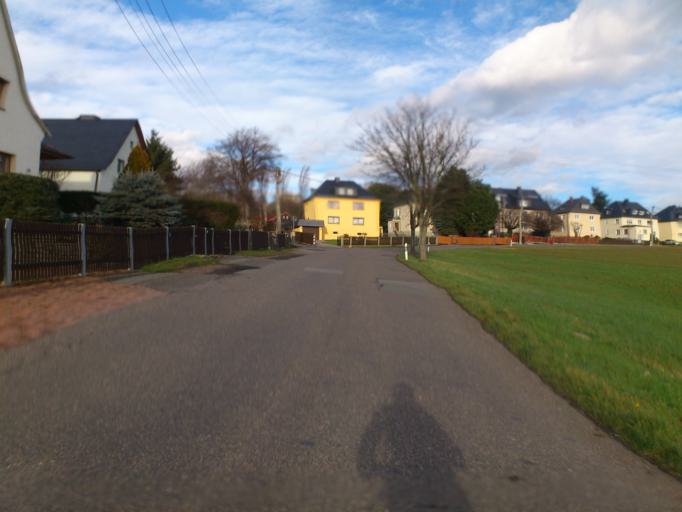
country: DE
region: Saxony
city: Neukirchen
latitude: 50.7801
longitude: 12.8789
